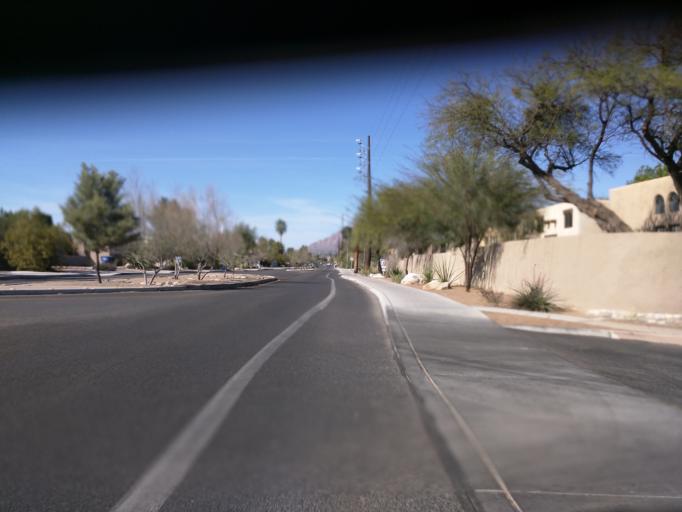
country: US
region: Arizona
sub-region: Pima County
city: Catalina Foothills
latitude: 32.2673
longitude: -110.9523
